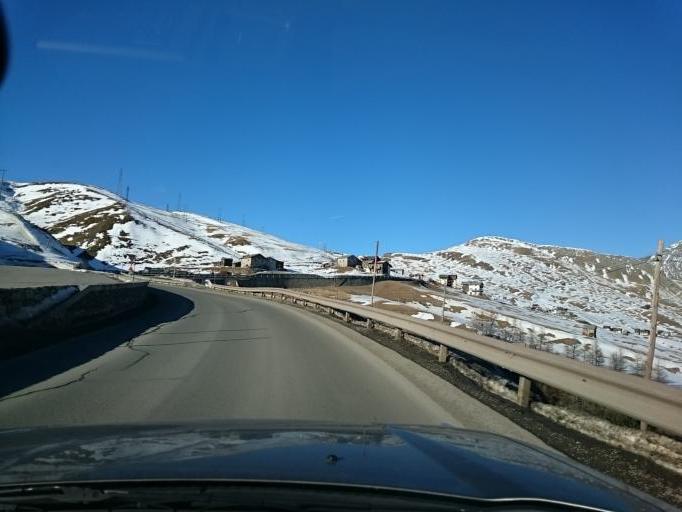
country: IT
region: Lombardy
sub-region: Provincia di Sondrio
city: Livigno
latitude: 46.5307
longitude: 10.1724
